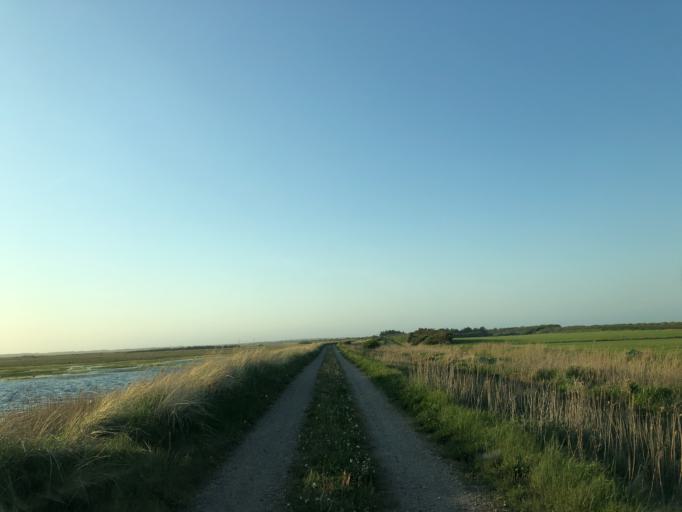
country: DK
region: Central Jutland
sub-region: Ringkobing-Skjern Kommune
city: Ringkobing
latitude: 56.2216
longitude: 8.1658
